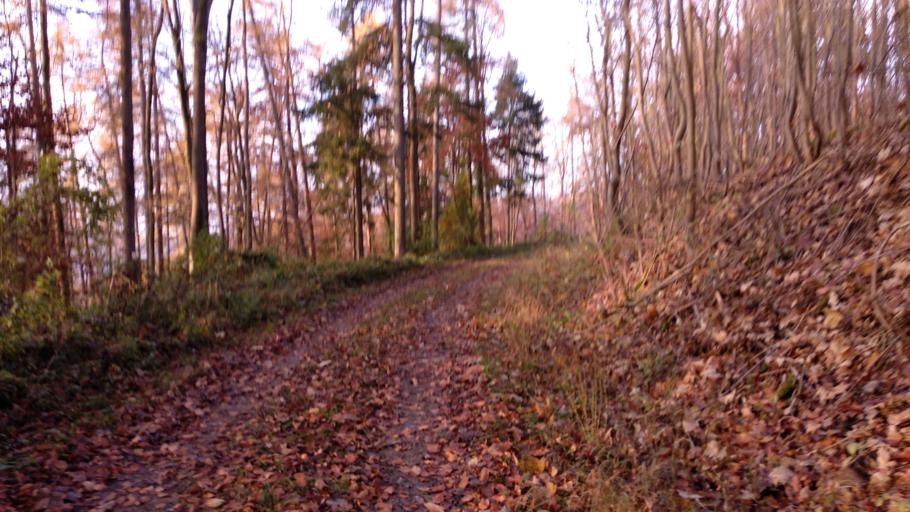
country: DE
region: North Rhine-Westphalia
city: Beverungen
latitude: 51.6617
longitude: 9.3456
